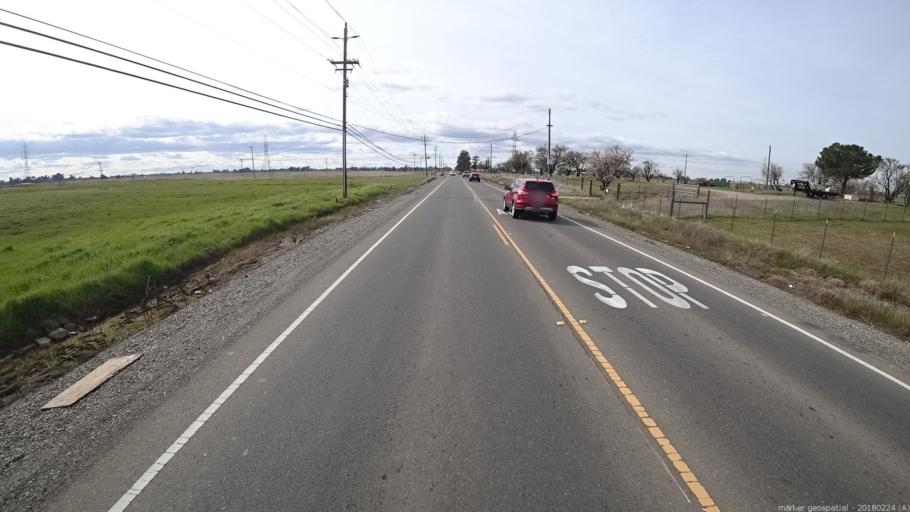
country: US
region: California
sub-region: Sacramento County
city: Rio Linda
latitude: 38.7143
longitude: -121.4281
